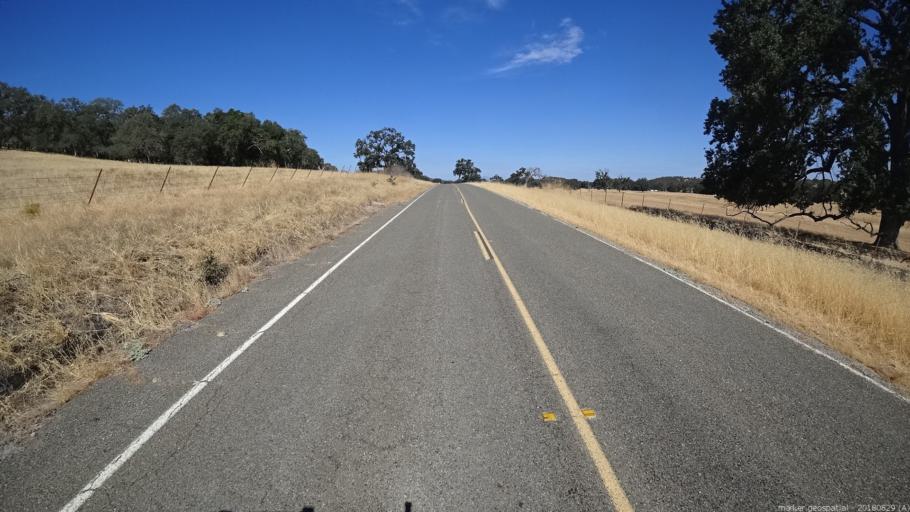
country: US
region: California
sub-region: San Luis Obispo County
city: Lake Nacimiento
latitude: 35.8246
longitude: -121.0150
